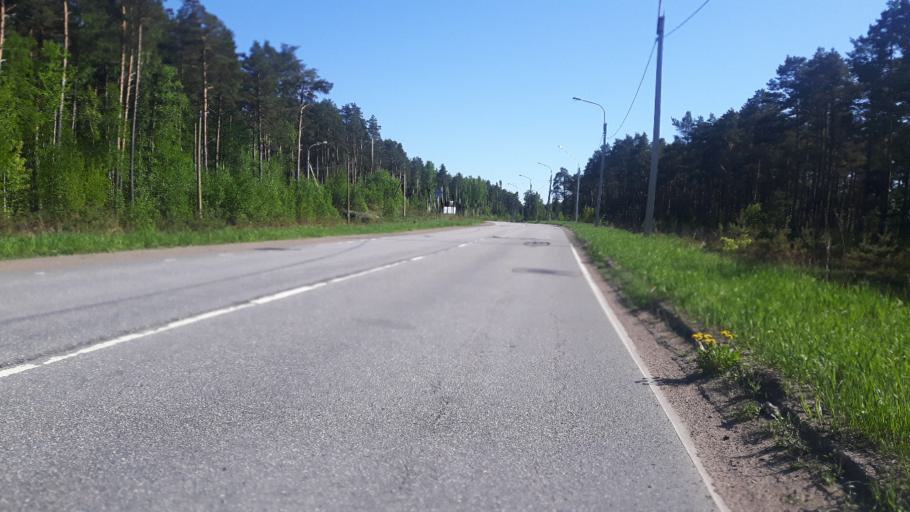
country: RU
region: Leningrad
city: Sosnovyy Bor
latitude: 60.2030
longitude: 29.0060
